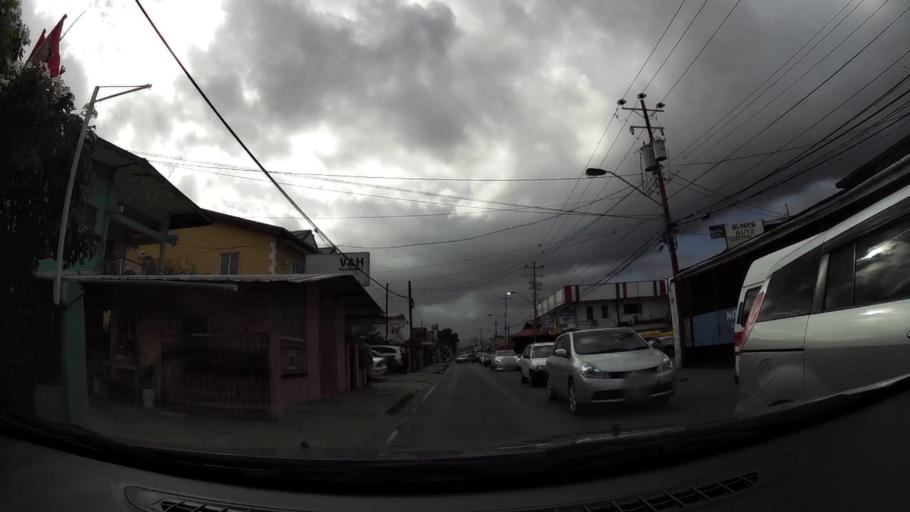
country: TT
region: Tunapuna/Piarco
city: Paradise
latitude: 10.6457
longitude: -61.3708
